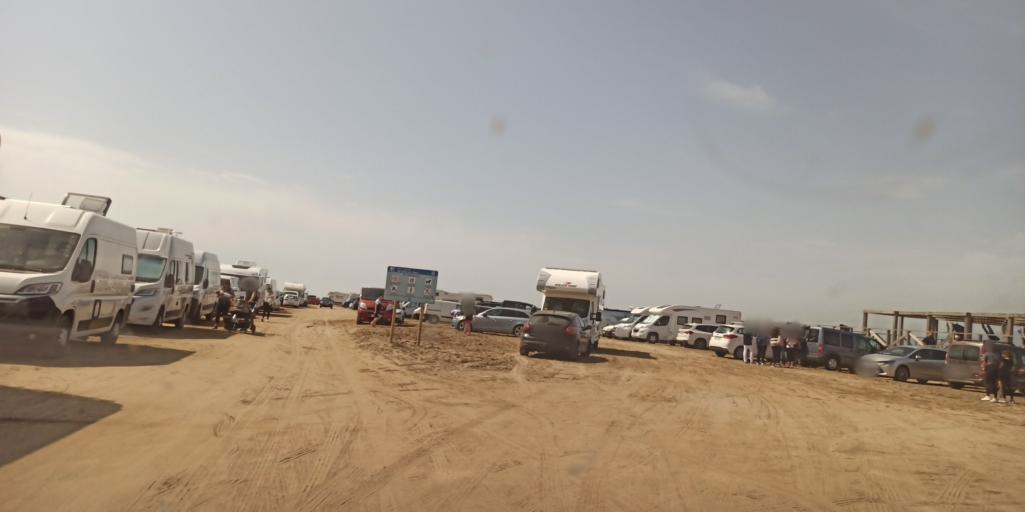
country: ES
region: Catalonia
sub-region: Provincia de Tarragona
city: Deltebre
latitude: 40.6296
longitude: 0.7424
